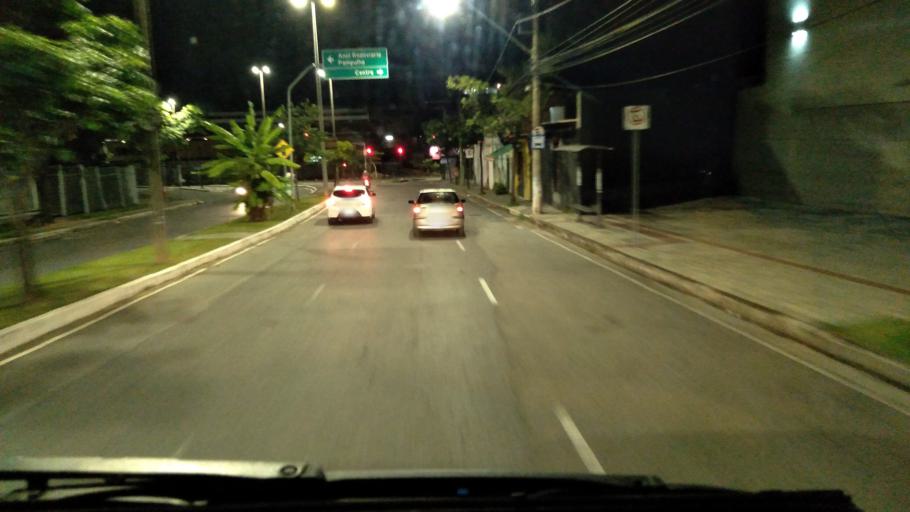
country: BR
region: Minas Gerais
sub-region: Belo Horizonte
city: Belo Horizonte
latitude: -19.8917
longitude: -43.9671
